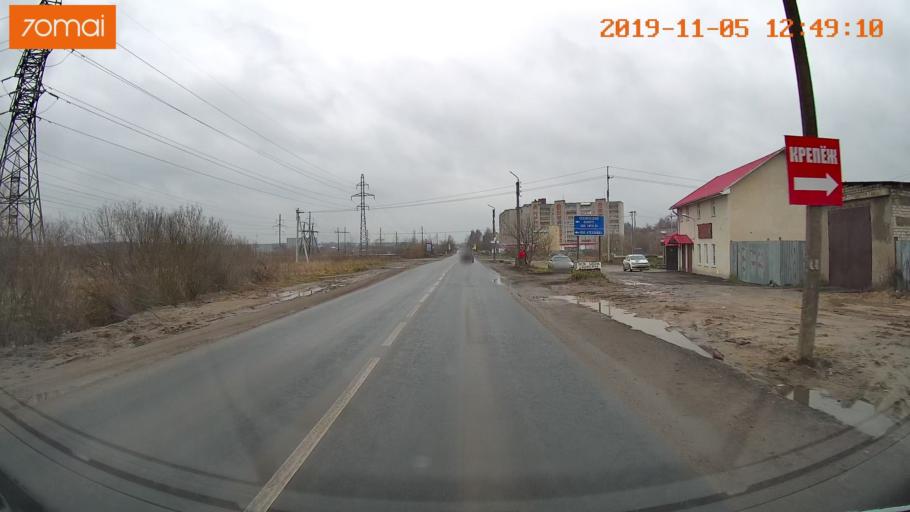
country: RU
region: Ivanovo
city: Kokhma
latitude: 56.9564
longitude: 41.1026
